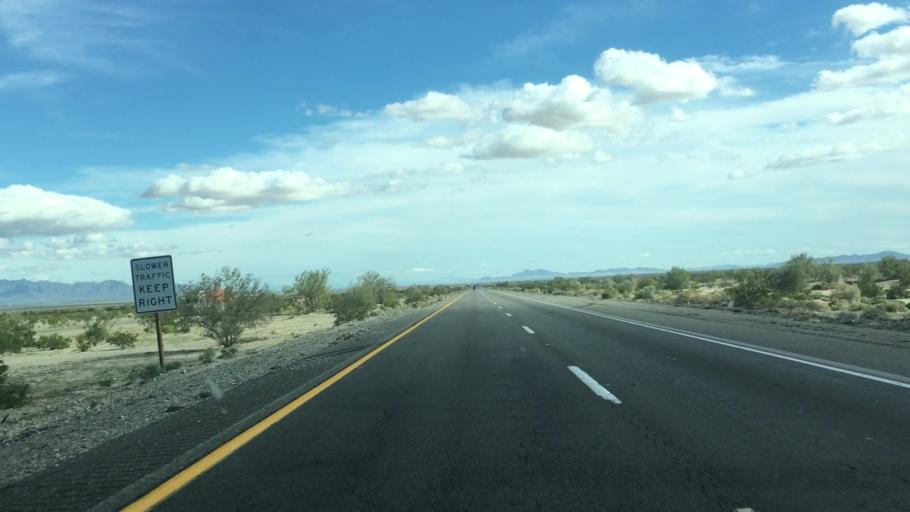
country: US
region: California
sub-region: Riverside County
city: Mesa Verde
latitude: 33.6542
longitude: -115.1484
